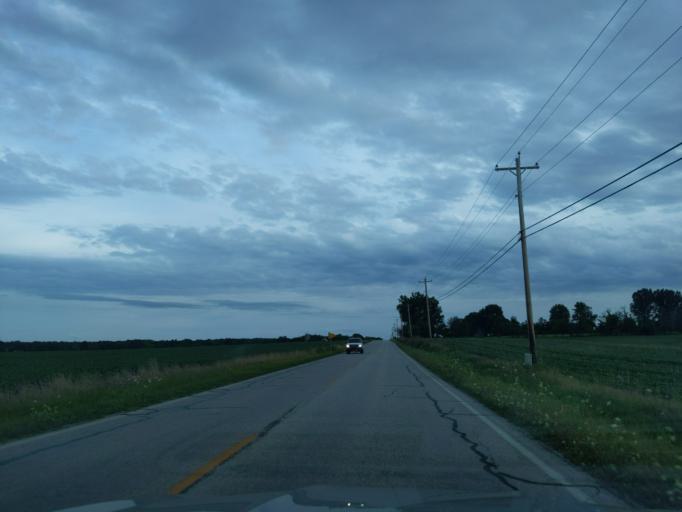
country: US
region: Indiana
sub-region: Ripley County
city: Sunman
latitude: 39.2584
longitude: -85.0945
